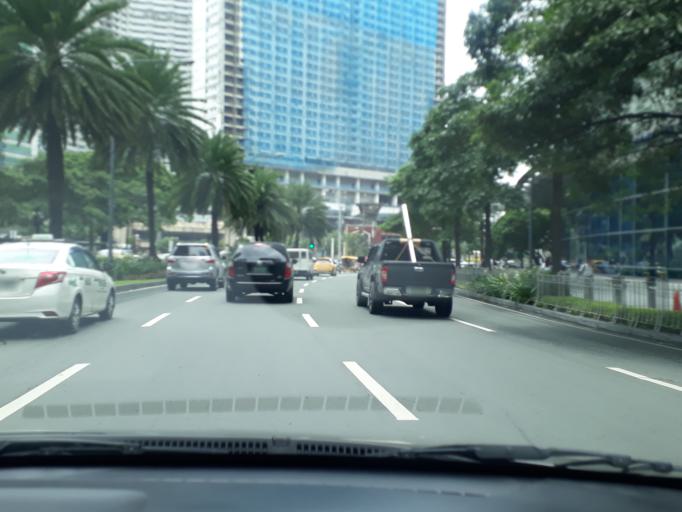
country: PH
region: Metro Manila
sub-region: Makati City
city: Makati City
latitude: 14.5600
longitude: 121.0159
